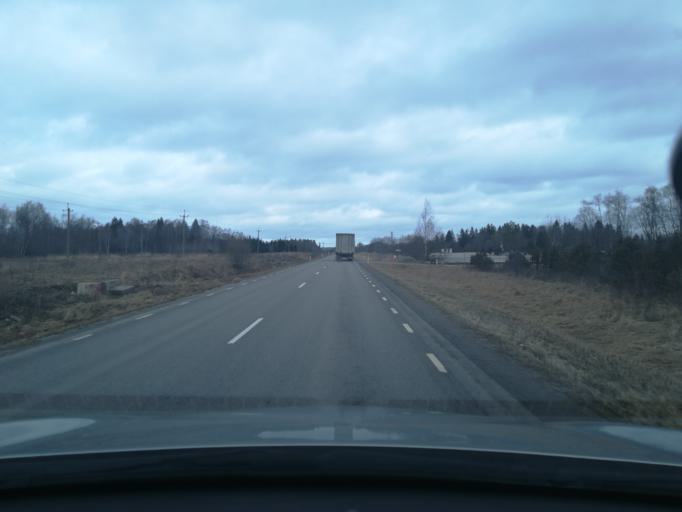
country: EE
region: Harju
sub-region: Harku vald
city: Tabasalu
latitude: 59.4099
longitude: 24.5460
